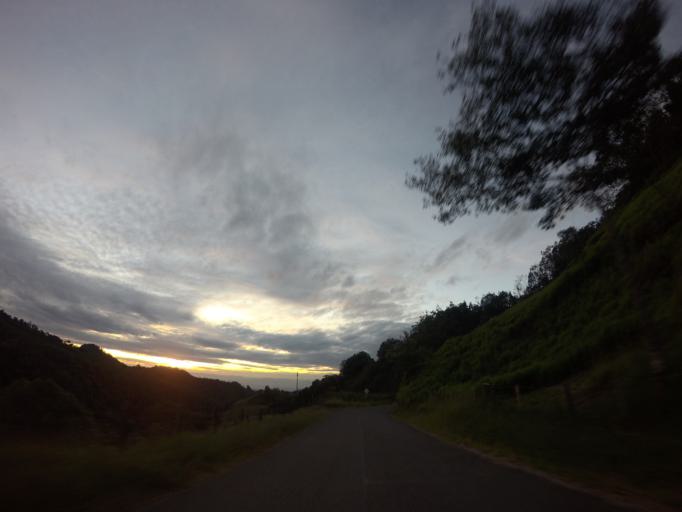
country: CO
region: Caldas
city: Manzanares
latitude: 5.2698
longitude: -75.1327
